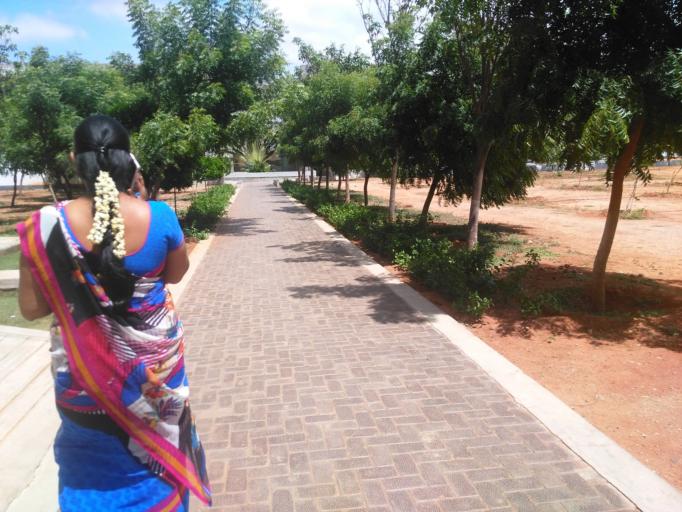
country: IN
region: Tamil Nadu
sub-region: Coimbatore
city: Sulur
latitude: 11.0766
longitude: 77.1430
